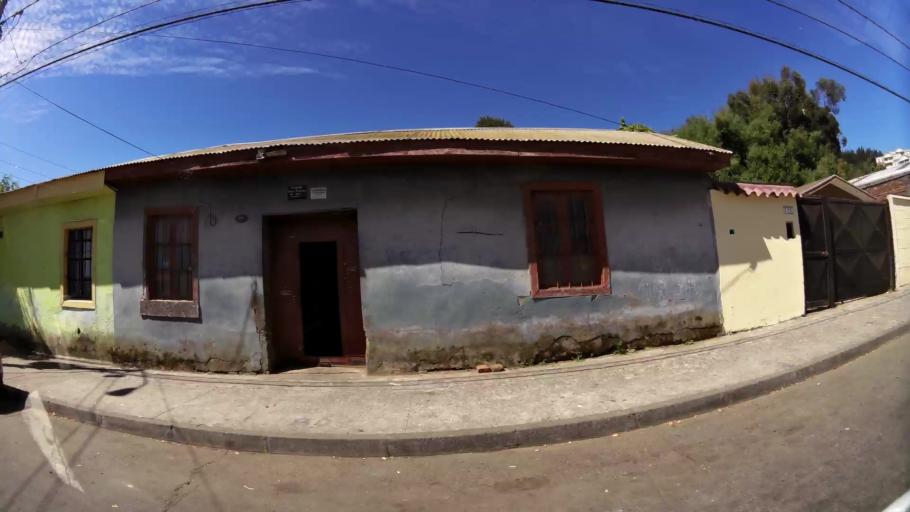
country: CL
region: Biobio
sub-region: Provincia de Concepcion
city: Penco
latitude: -36.7399
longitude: -72.9908
